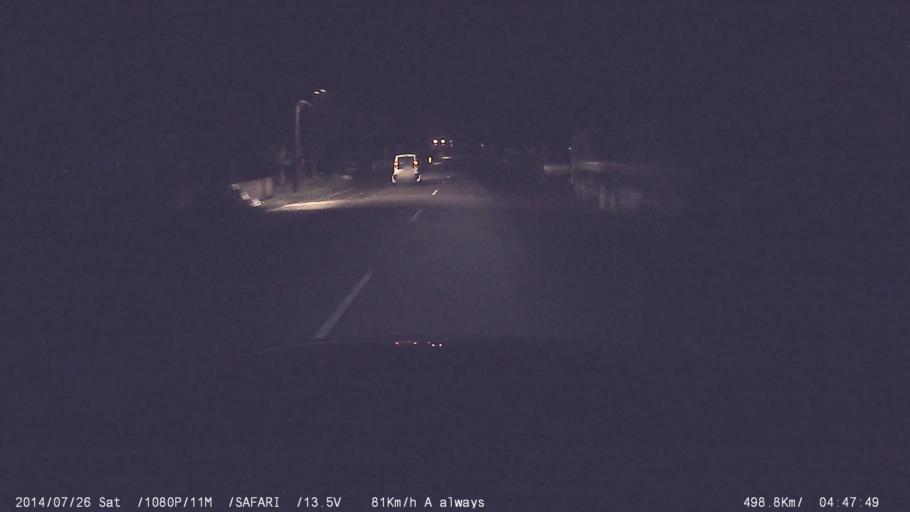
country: IN
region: Kerala
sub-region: Ernakulam
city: Angamali
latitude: 10.1742
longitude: 76.4245
